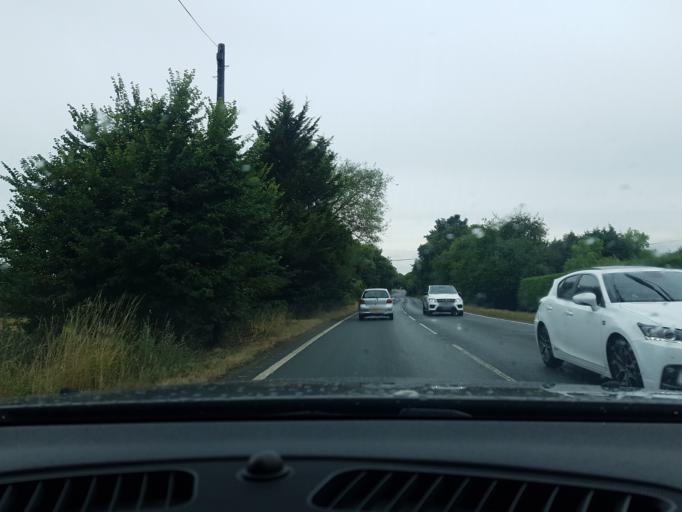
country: GB
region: England
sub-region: Hampshire
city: Odiham
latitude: 51.2552
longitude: -0.9205
